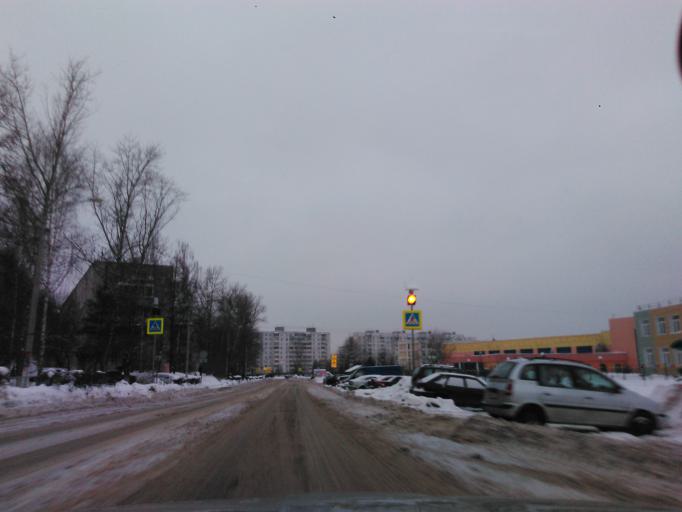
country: RU
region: Moskovskaya
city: Yakhroma
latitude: 56.2808
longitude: 37.4896
